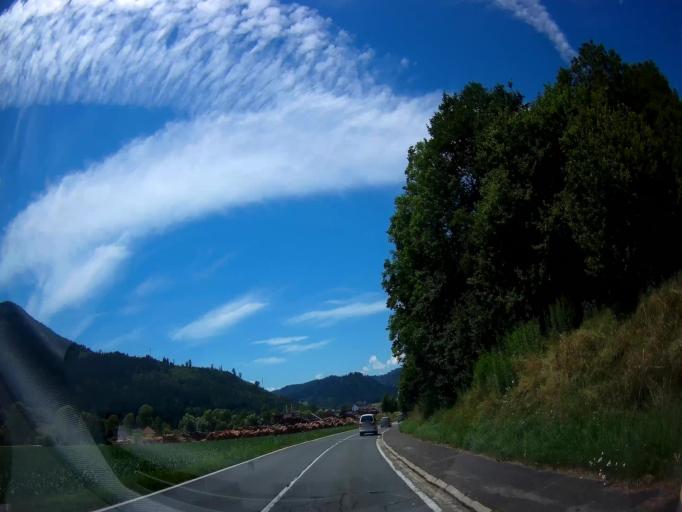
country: AT
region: Carinthia
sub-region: Politischer Bezirk Sankt Veit an der Glan
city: Strassburg
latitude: 46.8944
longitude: 14.3443
